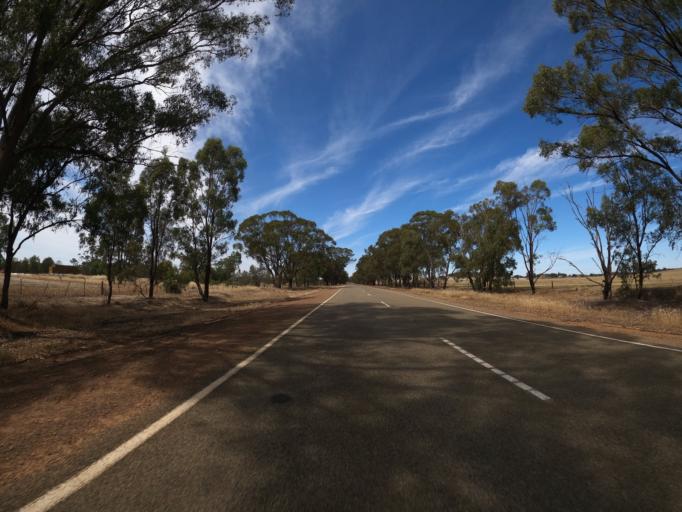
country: AU
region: Victoria
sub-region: Benalla
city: Benalla
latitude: -36.3092
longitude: 145.9583
